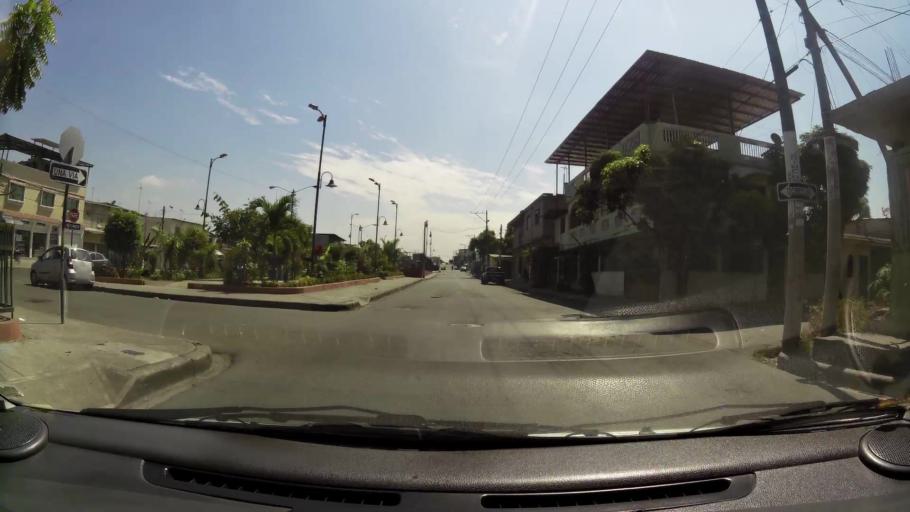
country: EC
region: Guayas
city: Guayaquil
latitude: -2.1249
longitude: -79.9226
